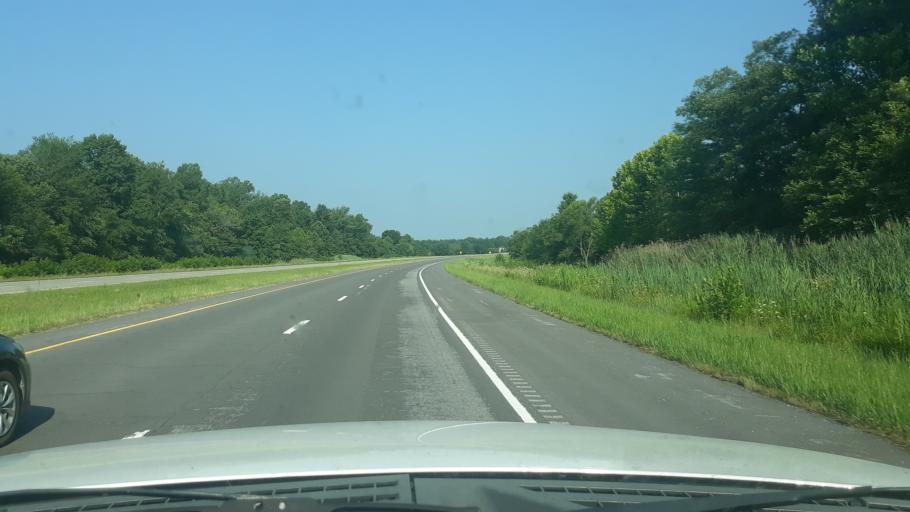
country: US
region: Illinois
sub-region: Saline County
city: Carrier Mills
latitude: 37.7346
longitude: -88.6977
